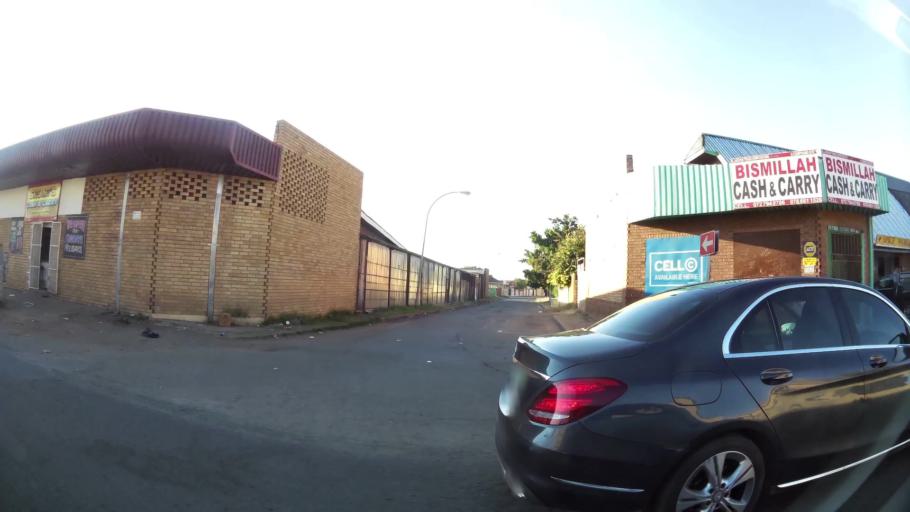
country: ZA
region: Northern Cape
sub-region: Frances Baard District Municipality
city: Kimberley
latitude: -28.7360
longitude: 24.7632
